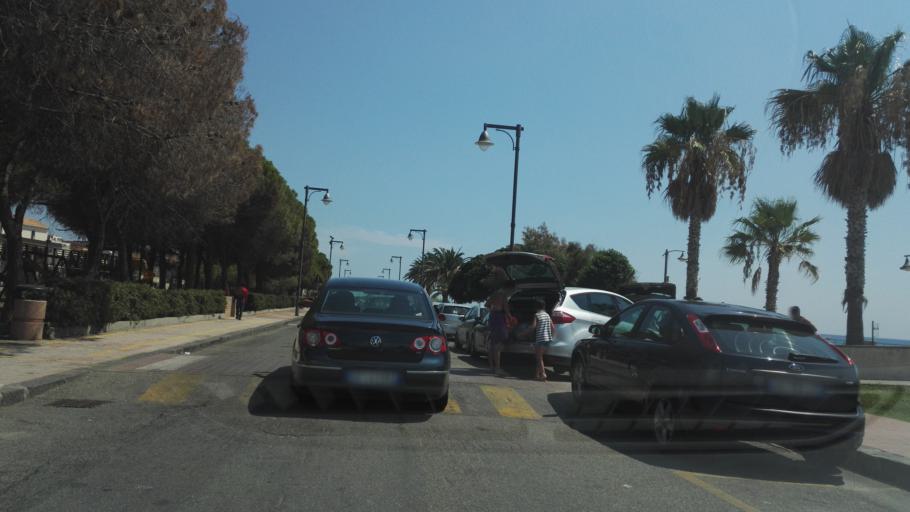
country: IT
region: Calabria
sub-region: Provincia di Reggio Calabria
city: Roccella Ionica
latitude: 38.3214
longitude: 16.4066
